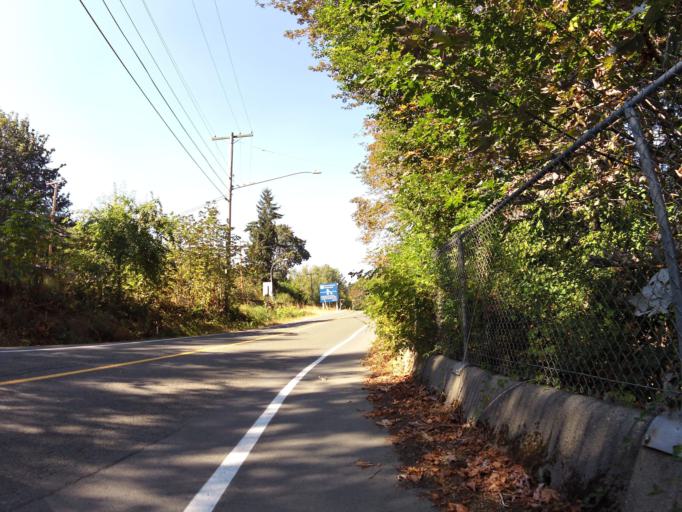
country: CA
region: British Columbia
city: North Saanich
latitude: 48.6155
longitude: -123.5209
